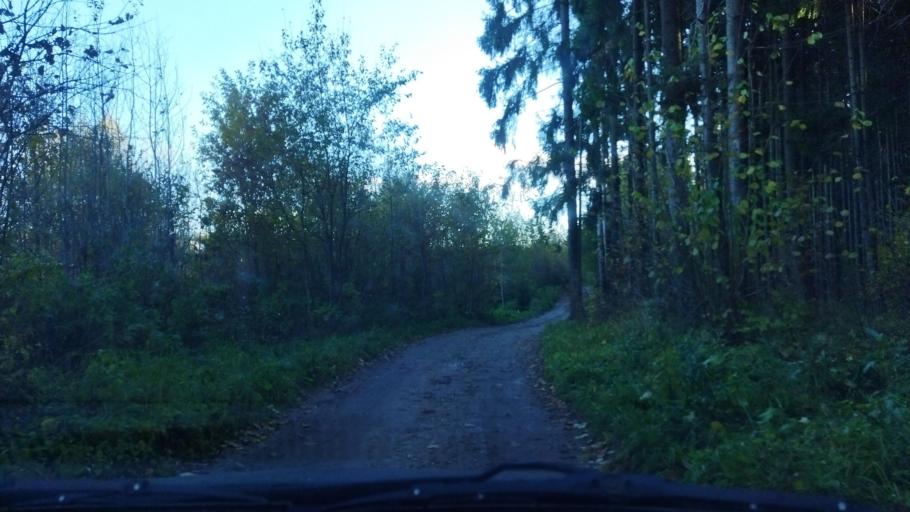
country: BY
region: Minsk
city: Slabada
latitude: 53.9890
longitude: 27.8899
